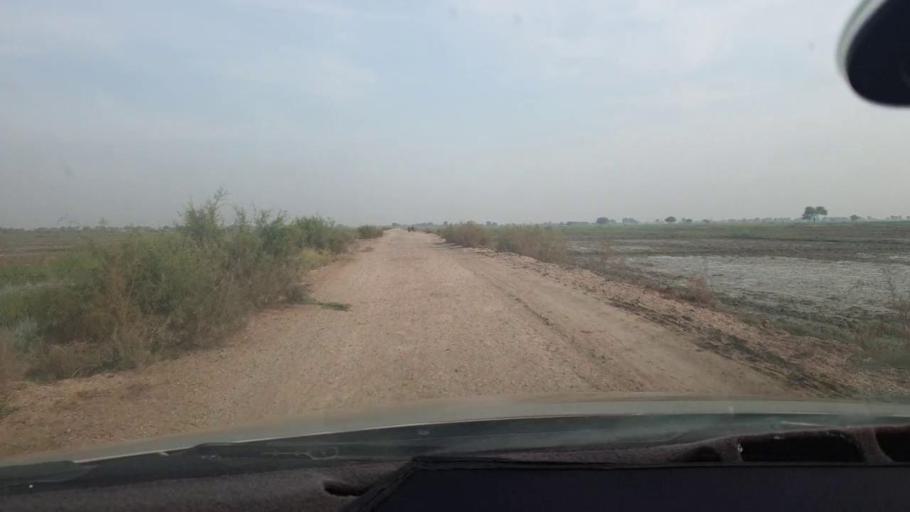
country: PK
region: Balochistan
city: Jhatpat
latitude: 28.3578
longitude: 68.4079
